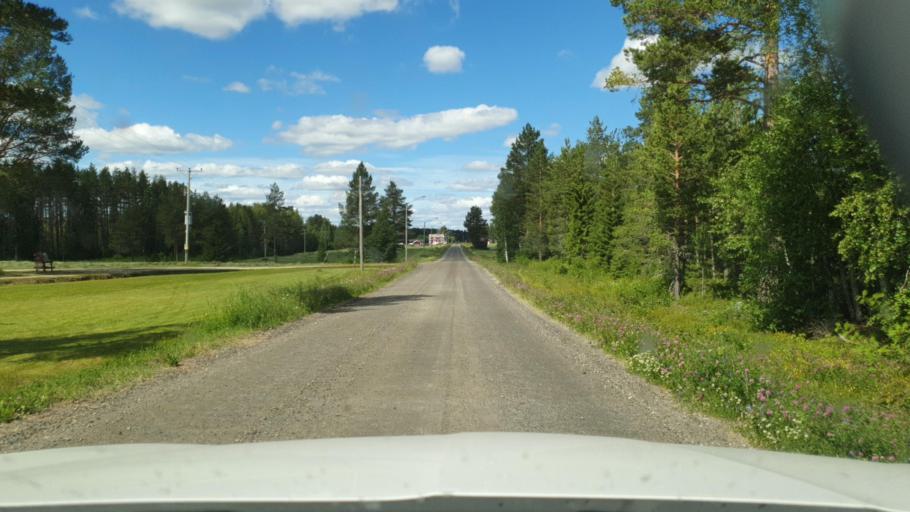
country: SE
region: Vaesterbotten
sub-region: Skelleftea Kommun
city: Backa
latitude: 65.1811
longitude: 21.0728
